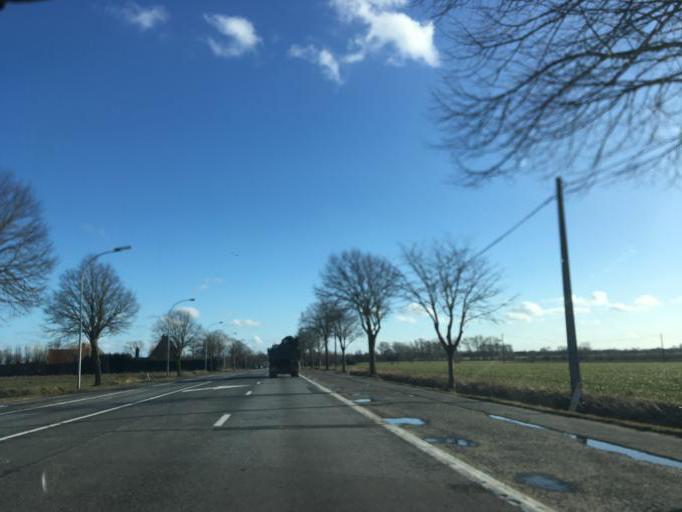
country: BE
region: Flanders
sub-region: Provincie West-Vlaanderen
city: Torhout
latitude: 51.0463
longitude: 3.1060
